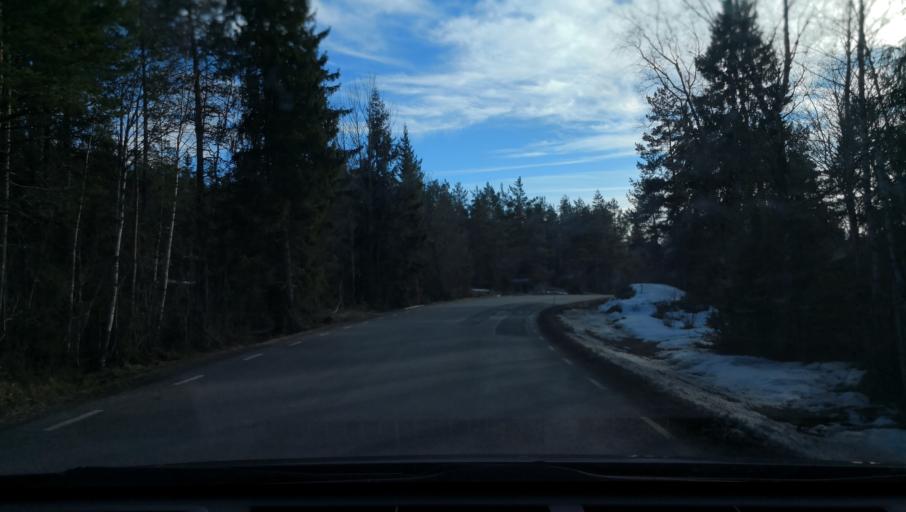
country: SE
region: Uppsala
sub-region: Osthammars Kommun
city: Osterbybruk
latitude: 60.2563
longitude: 17.9472
